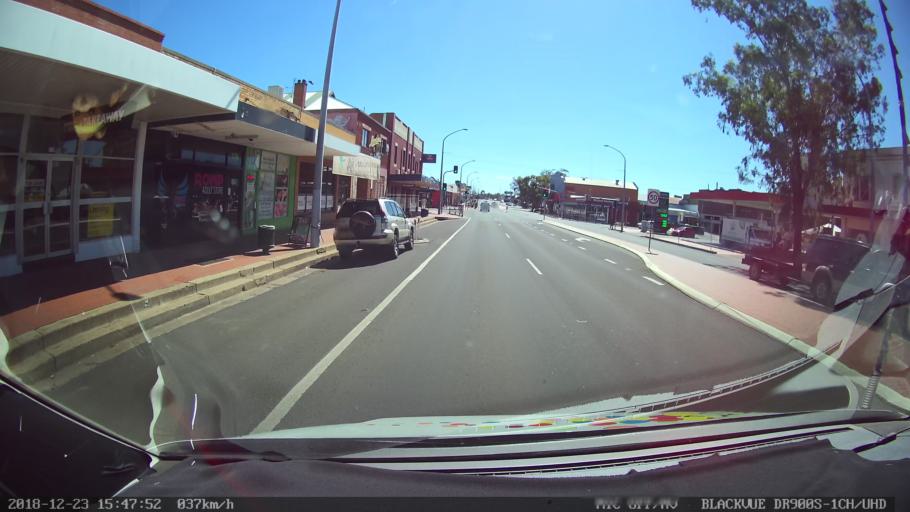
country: AU
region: New South Wales
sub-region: Tamworth Municipality
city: Tamworth
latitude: -31.0936
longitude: 150.9175
